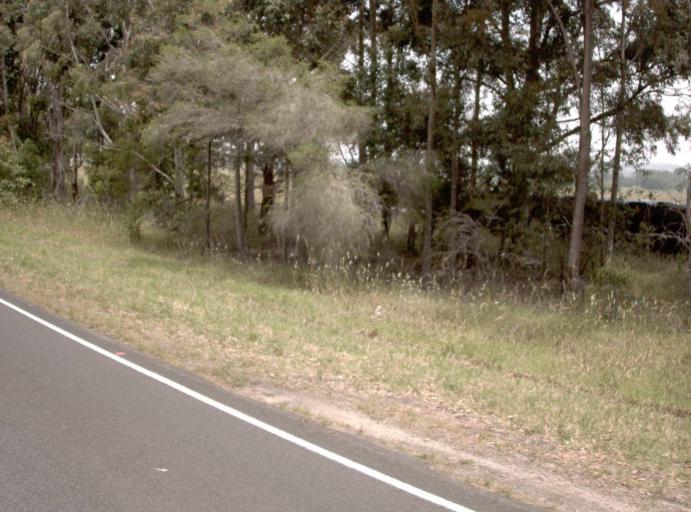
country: AU
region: Victoria
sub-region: Latrobe
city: Traralgon
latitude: -38.4688
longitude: 146.7179
